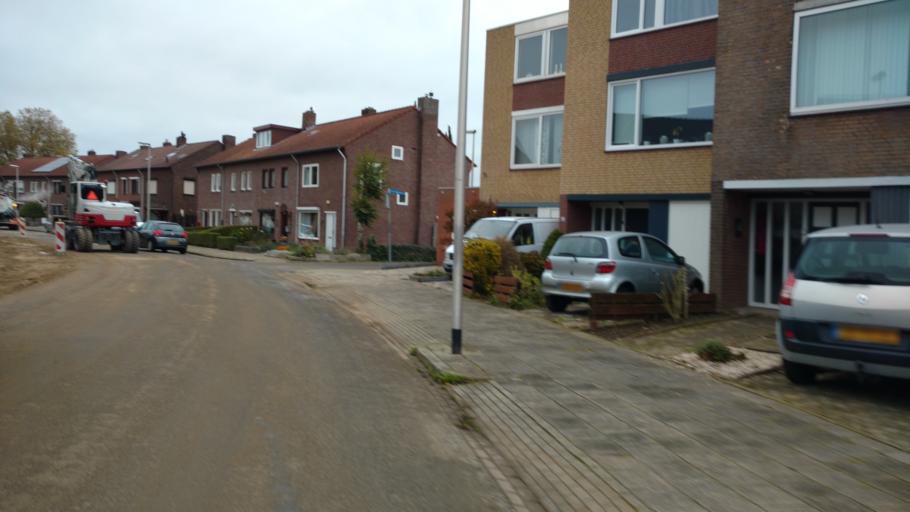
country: NL
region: Limburg
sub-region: Gemeente Heerlen
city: Heerlen
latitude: 50.8942
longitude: 5.9878
